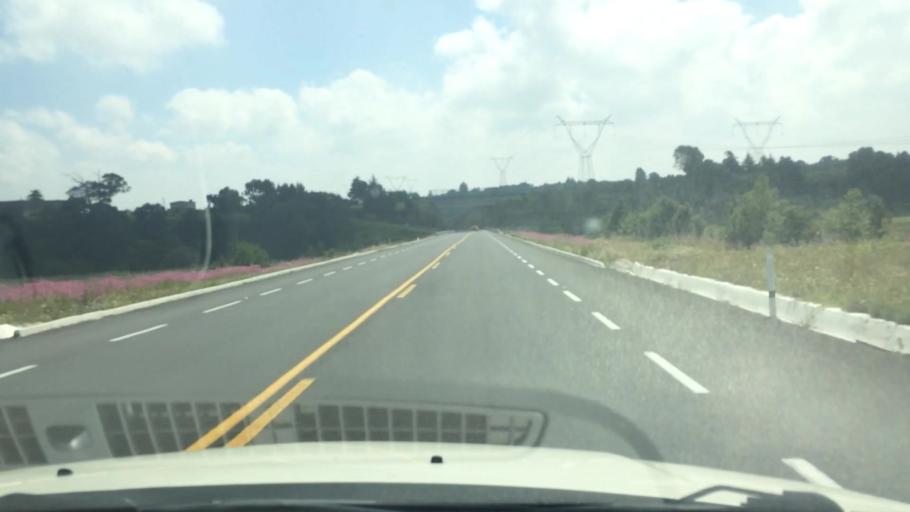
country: MX
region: Mexico
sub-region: Villa Victoria
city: Colonia Doctor Gustavo Baz
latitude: 19.3768
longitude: -99.8755
